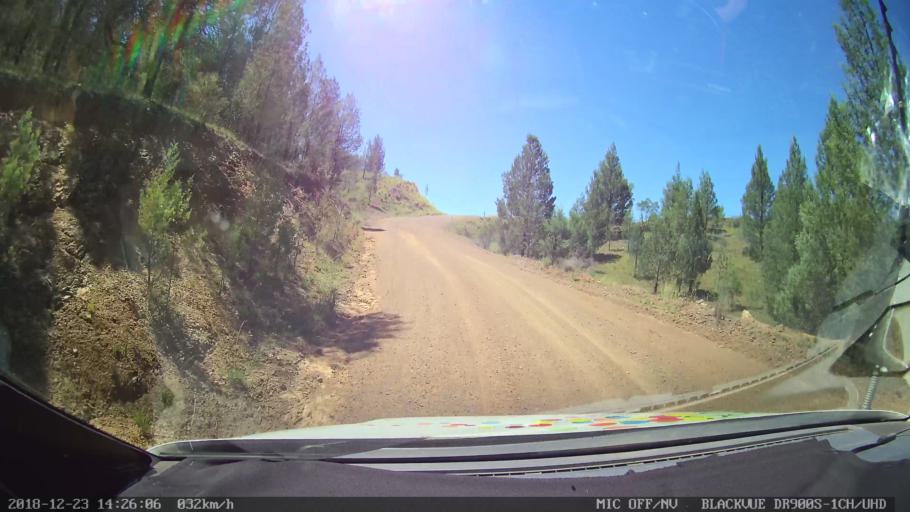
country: AU
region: New South Wales
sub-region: Tamworth Municipality
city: Manilla
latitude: -30.6244
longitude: 150.9534
